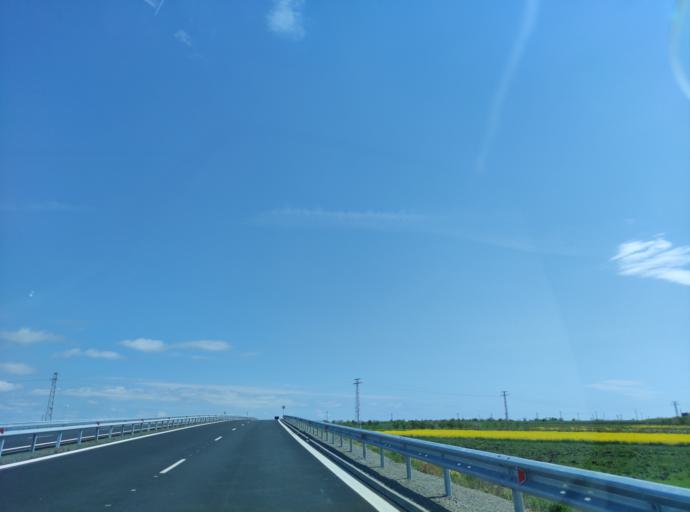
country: BG
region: Burgas
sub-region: Obshtina Pomorie
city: Pomorie
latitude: 42.5777
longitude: 27.5785
